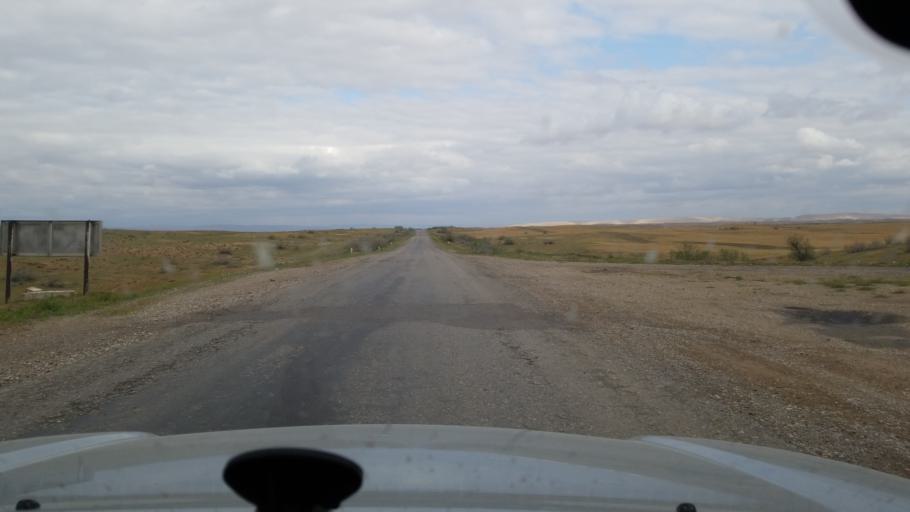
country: TM
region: Mary
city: Serhetabat
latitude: 35.9849
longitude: 62.6298
